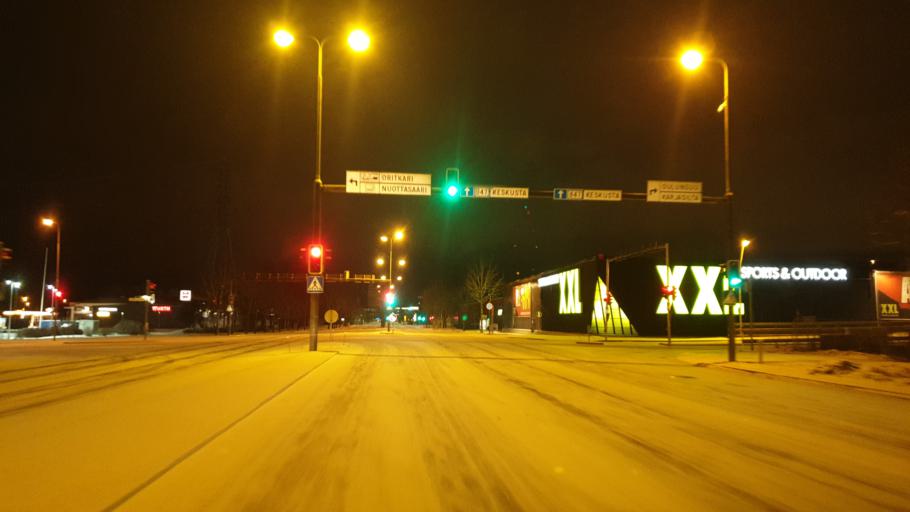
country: FI
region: Northern Ostrobothnia
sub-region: Oulu
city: Oulu
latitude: 64.9960
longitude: 25.4646
